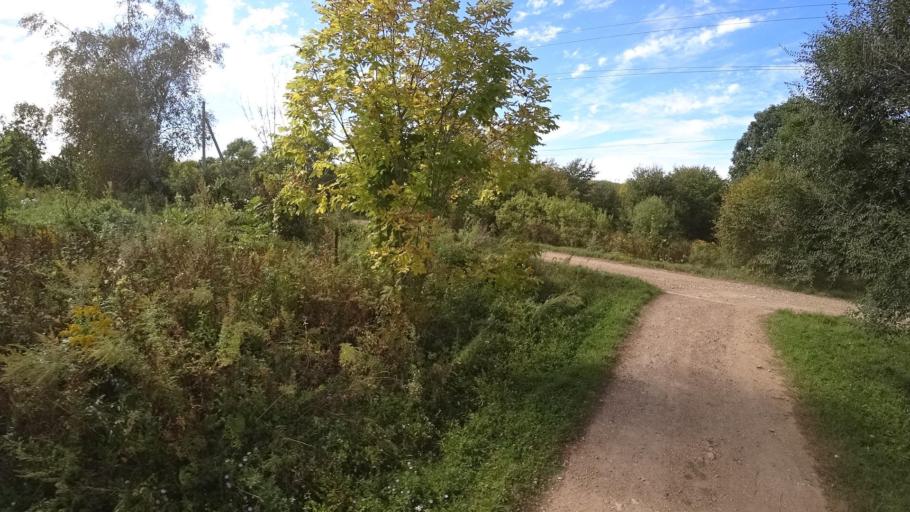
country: RU
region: Primorskiy
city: Yakovlevka
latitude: 44.3899
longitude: 133.6061
